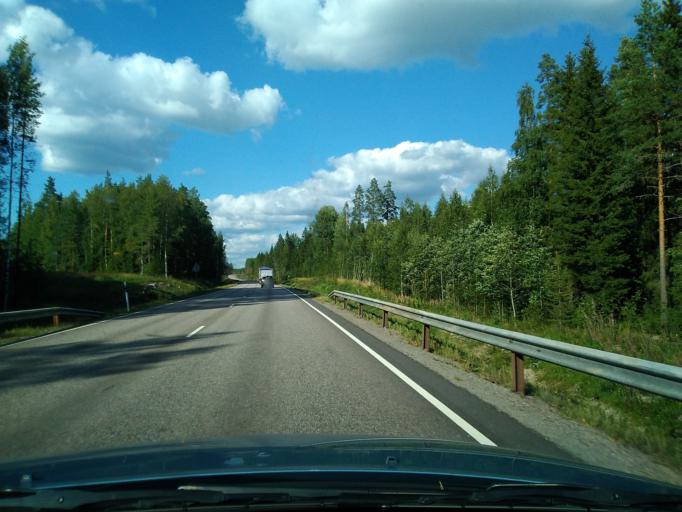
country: FI
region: Central Finland
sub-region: Keuruu
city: Keuruu
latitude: 62.1393
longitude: 24.7425
